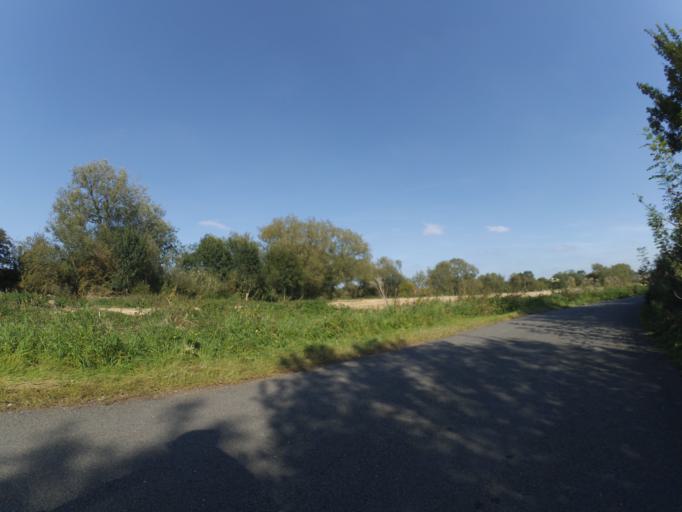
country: GB
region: England
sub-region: Warwickshire
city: Rugby
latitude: 52.4163
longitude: -1.2647
